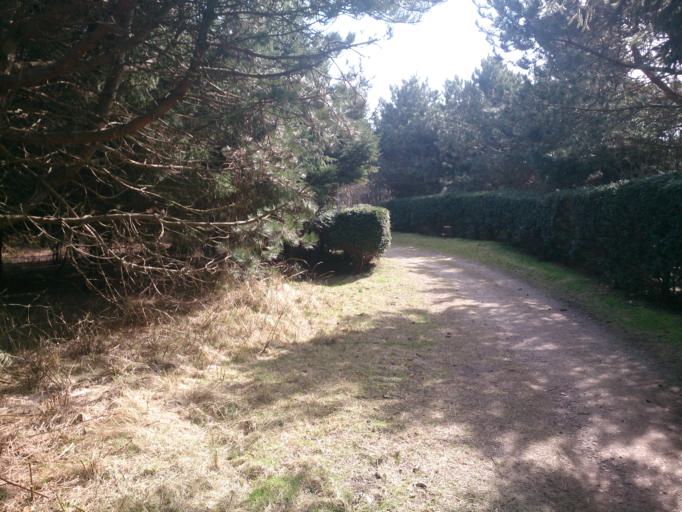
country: DE
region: Schleswig-Holstein
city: Utersum
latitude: 54.7016
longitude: 8.4025
